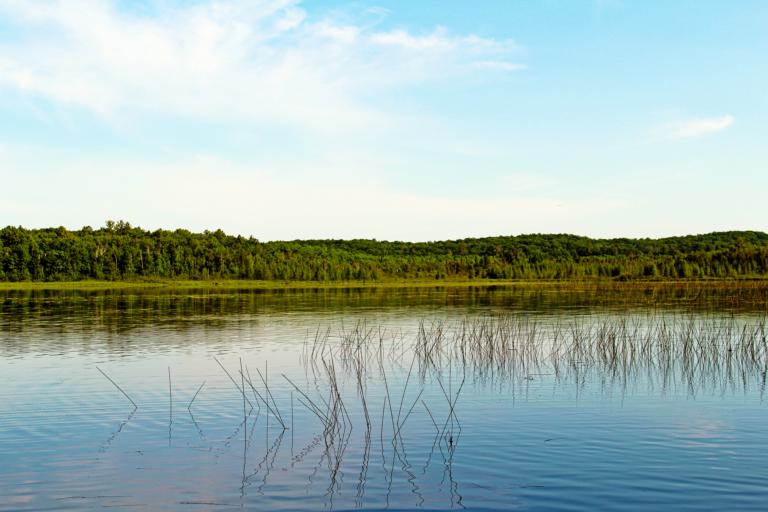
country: US
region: Wisconsin
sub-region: Sawyer County
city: Hayward
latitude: 46.0145
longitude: -91.6618
